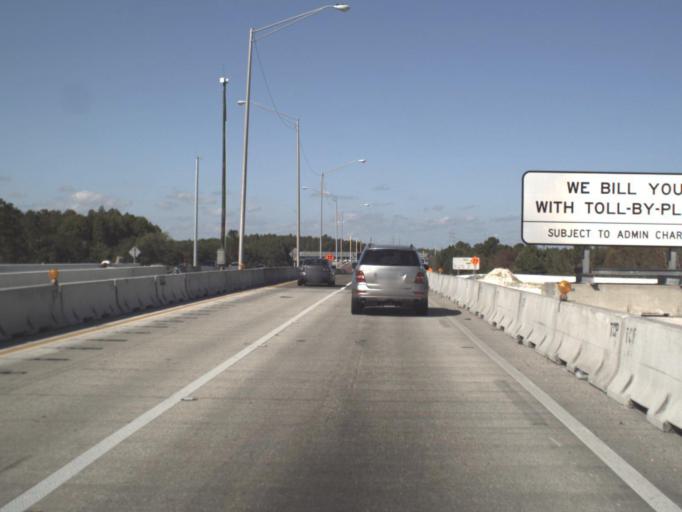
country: US
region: Florida
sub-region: Hillsborough County
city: Town 'n' Country
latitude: 28.0368
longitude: -82.5493
